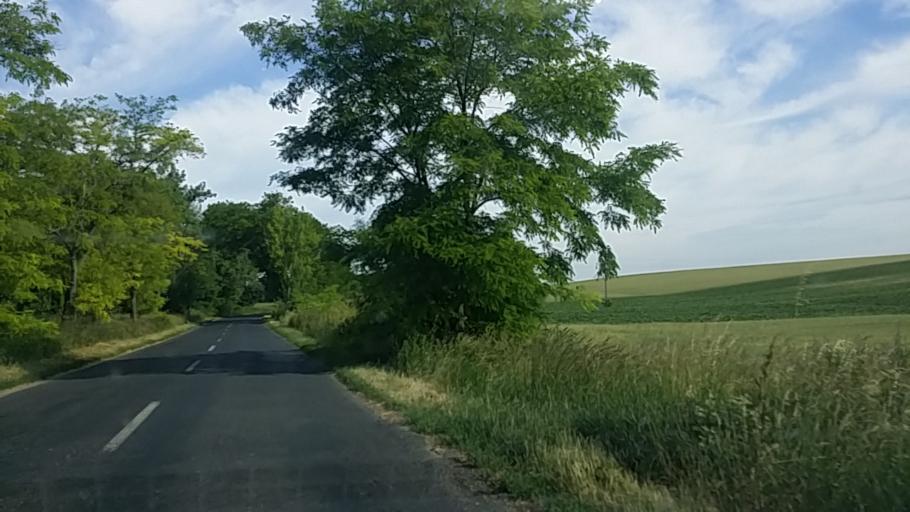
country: HU
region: Komarom-Esztergom
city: Bajna
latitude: 47.6657
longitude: 18.5819
